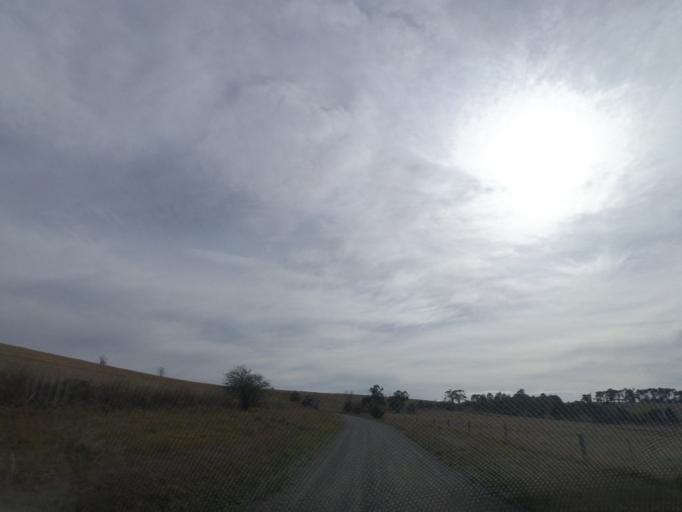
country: AU
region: Victoria
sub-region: Yarra Ranges
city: Yarra Glen
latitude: -37.6442
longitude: 145.4223
